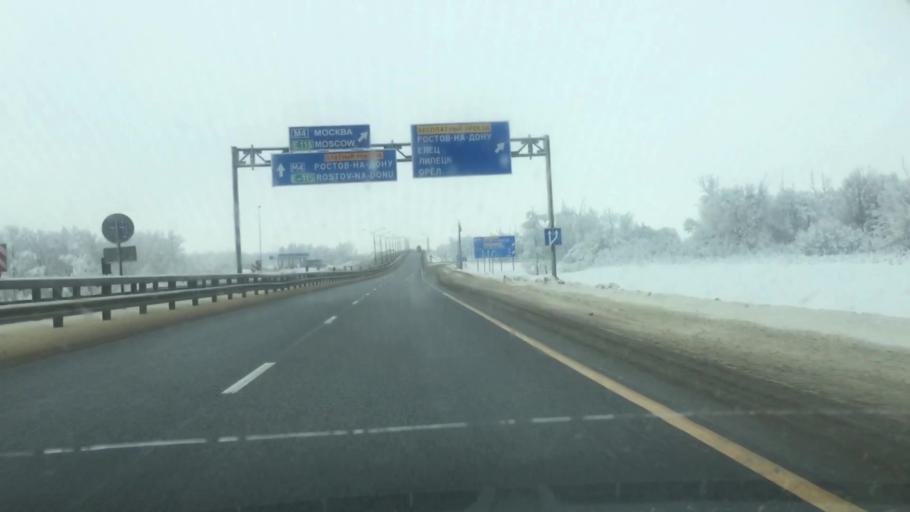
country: RU
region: Lipetsk
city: Yelets
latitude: 52.5541
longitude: 38.7161
